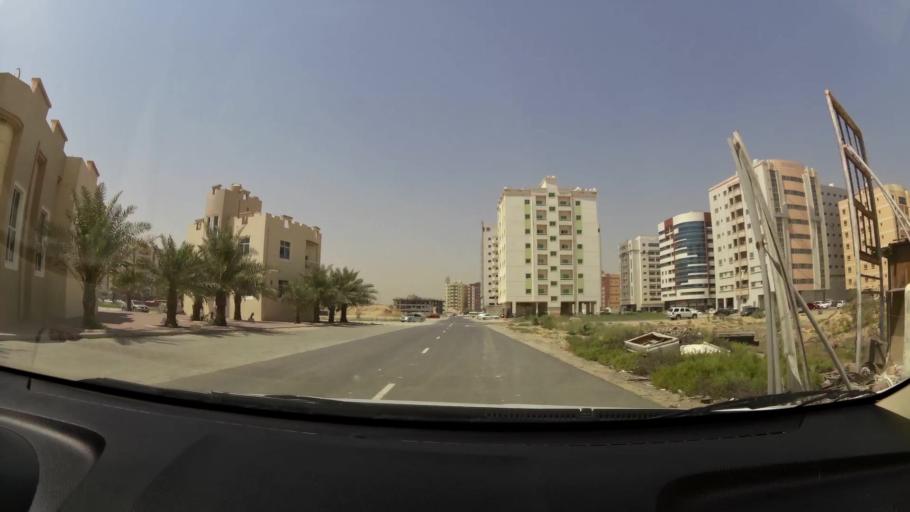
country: AE
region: Ajman
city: Ajman
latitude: 25.4100
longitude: 55.5134
